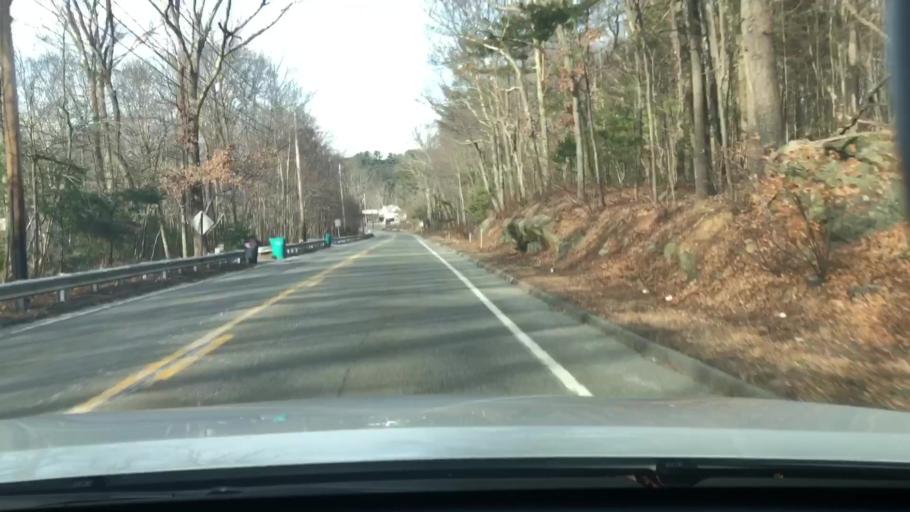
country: US
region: Massachusetts
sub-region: Worcester County
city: Upton
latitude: 42.1685
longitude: -71.5947
